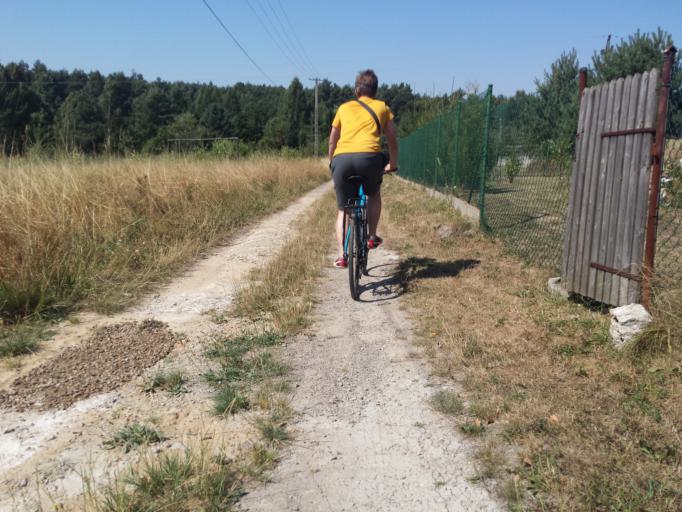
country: PL
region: Swietokrzyskie
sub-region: Powiat kielecki
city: Daleszyce
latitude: 50.8030
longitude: 20.7646
